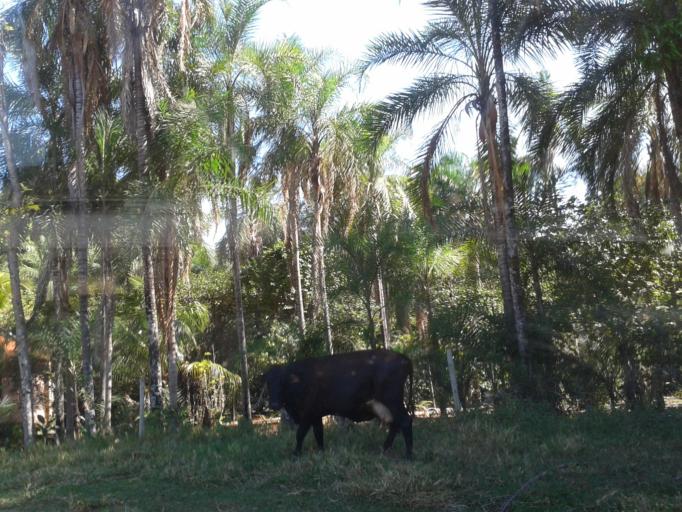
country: BR
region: Minas Gerais
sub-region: Campina Verde
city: Campina Verde
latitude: -19.4481
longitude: -49.5672
